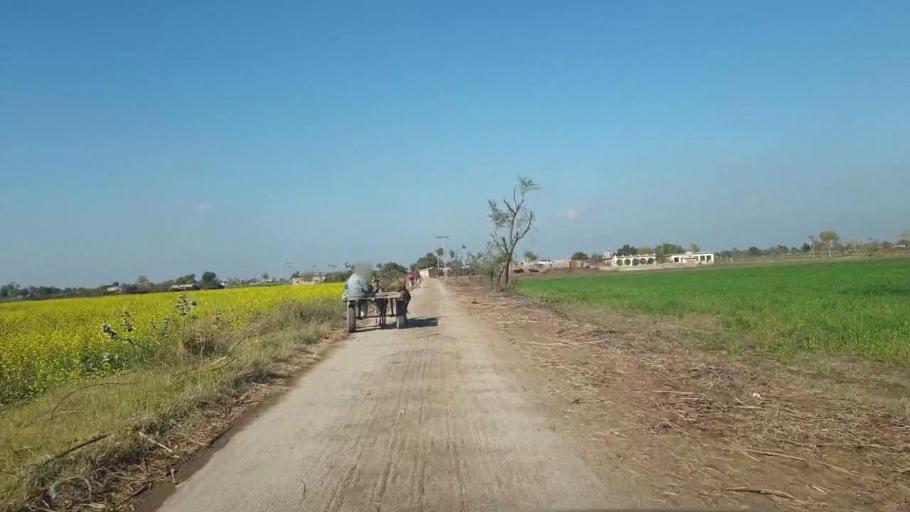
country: PK
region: Sindh
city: Shahdadpur
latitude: 25.9310
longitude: 68.5302
